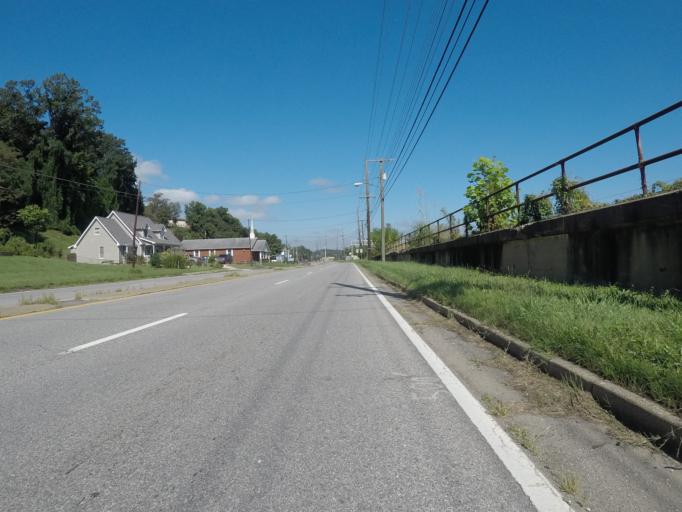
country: US
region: Ohio
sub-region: Lawrence County
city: South Point
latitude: 38.4309
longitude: -82.6039
